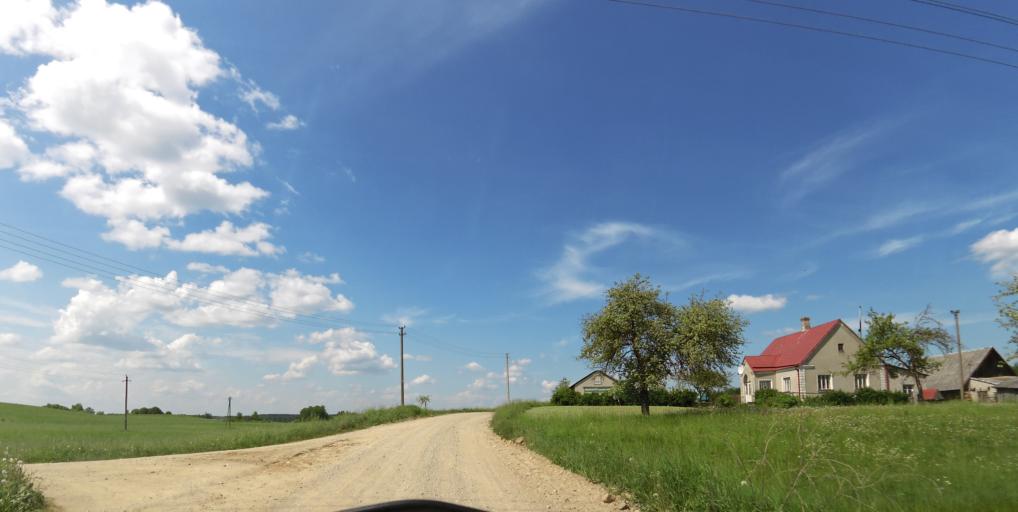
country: LT
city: Grigiskes
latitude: 54.7476
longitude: 25.1098
